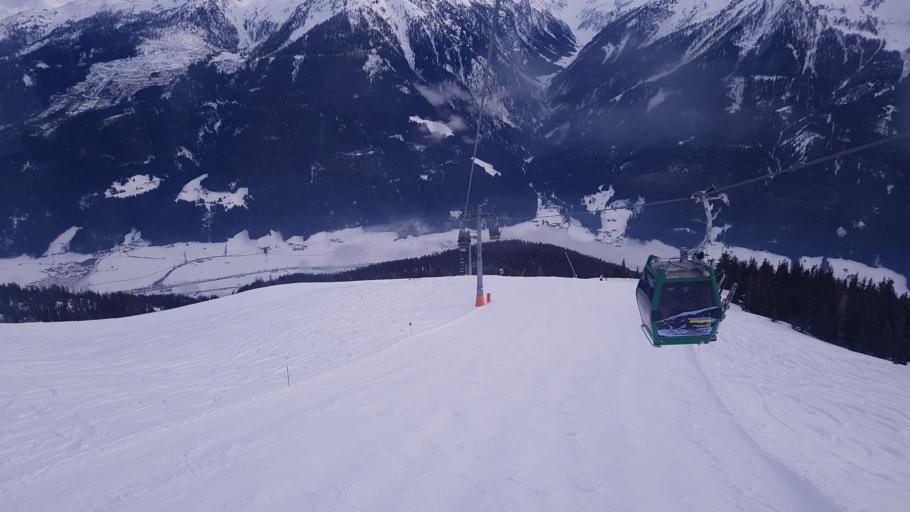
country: AT
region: Salzburg
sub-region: Politischer Bezirk Zell am See
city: Neukirchen am Grossvenediger
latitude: 47.2785
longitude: 12.2974
